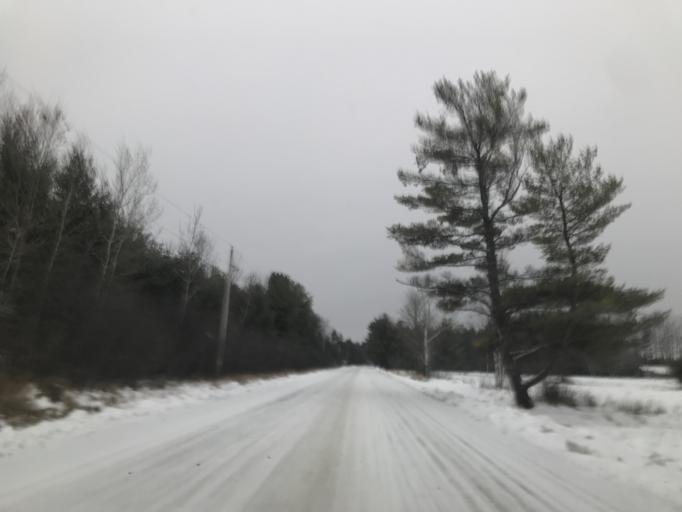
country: US
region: Wisconsin
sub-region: Marinette County
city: Peshtigo
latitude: 45.0518
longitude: -87.7199
